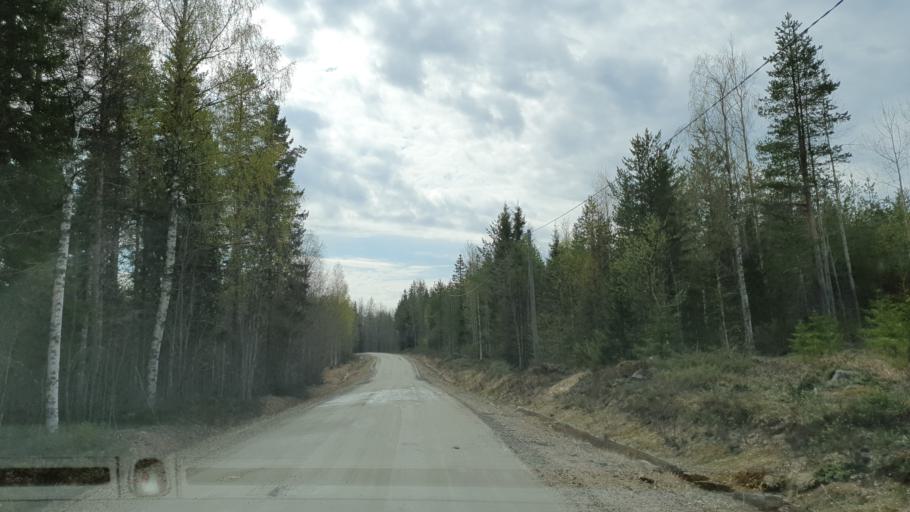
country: FI
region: Kainuu
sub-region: Kehys-Kainuu
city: Kuhmo
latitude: 64.1017
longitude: 29.9415
